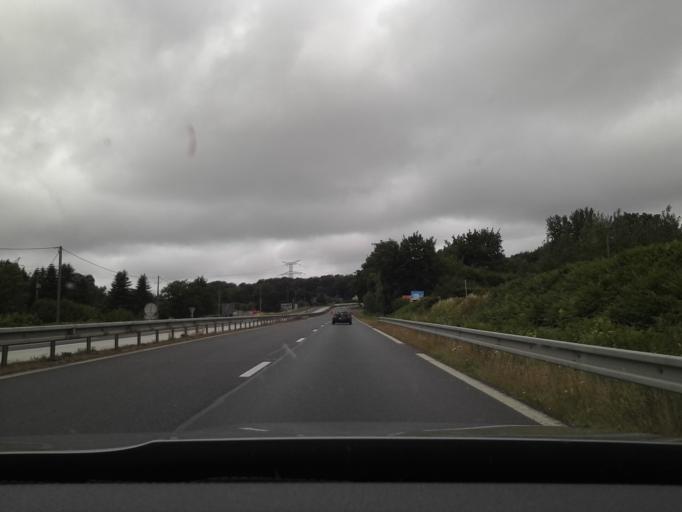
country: FR
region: Lower Normandy
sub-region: Departement de la Manche
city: Brix
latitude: 49.5449
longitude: -1.5543
